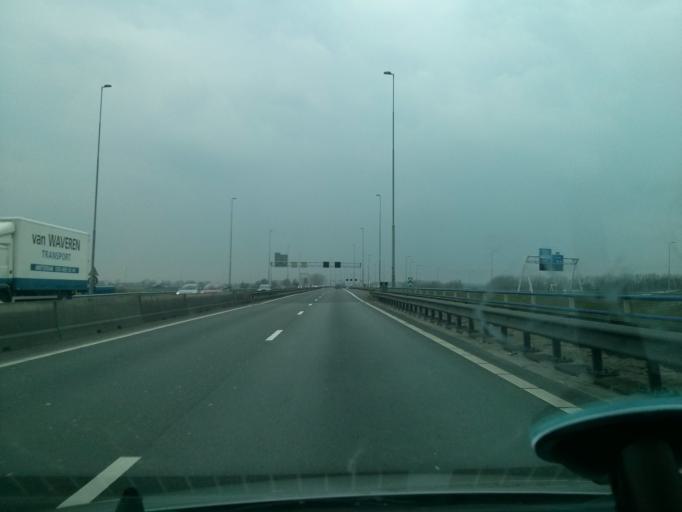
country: NL
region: North Holland
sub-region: Gemeente Amsterdam
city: Amsterdam-Zuidoost
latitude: 52.2861
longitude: 4.9484
